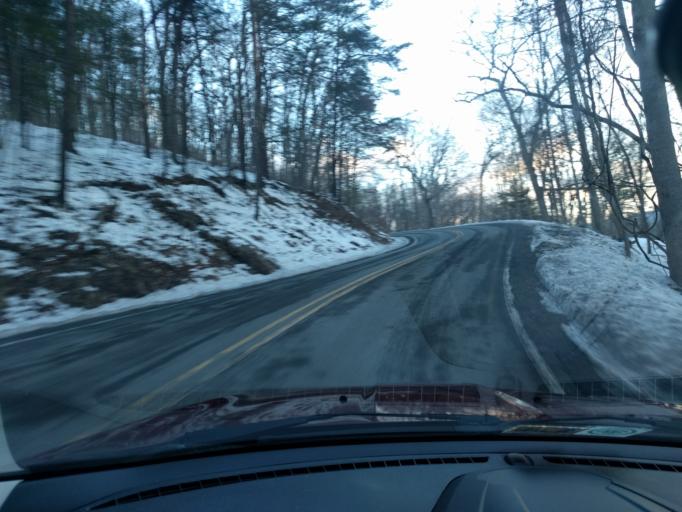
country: US
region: Virginia
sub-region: Bath County
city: Warm Springs
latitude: 38.0904
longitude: -79.8410
